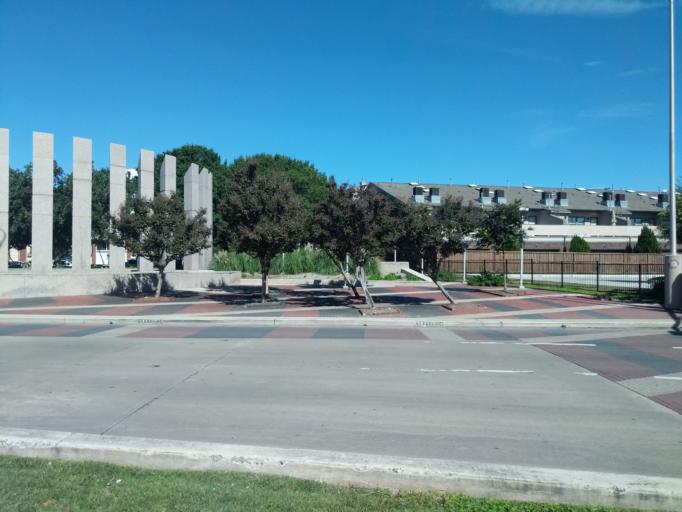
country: US
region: Texas
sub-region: Dallas County
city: Dallas
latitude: 32.7841
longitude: -96.7732
